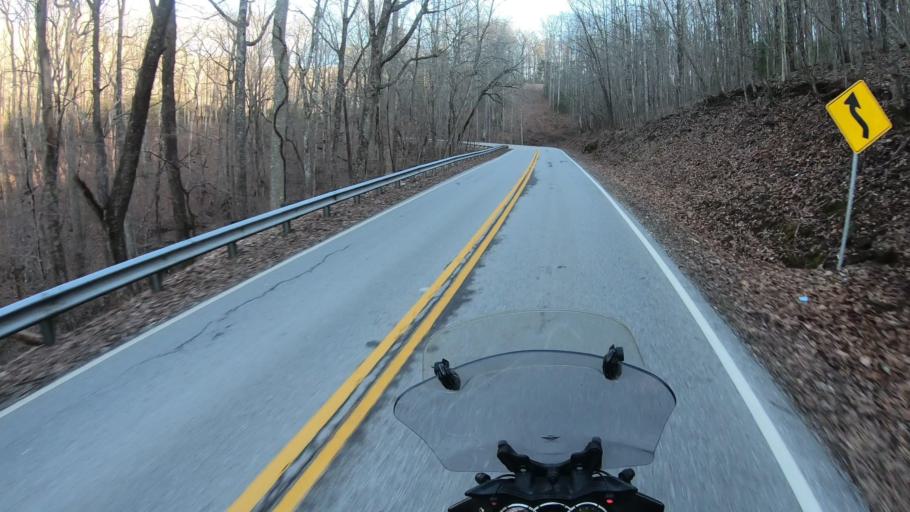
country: US
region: Georgia
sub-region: Union County
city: Blairsville
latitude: 34.7105
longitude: -84.0457
